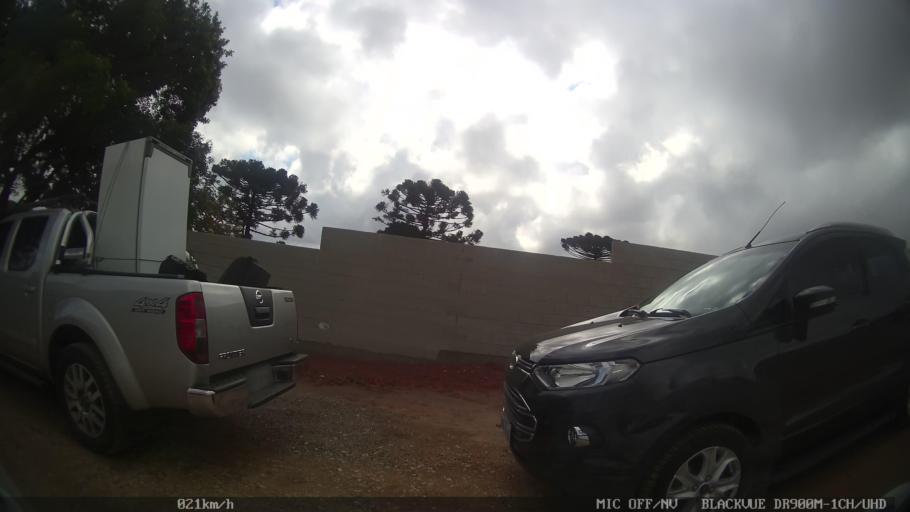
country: BR
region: Parana
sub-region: Colombo
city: Colombo
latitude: -25.3560
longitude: -49.2336
